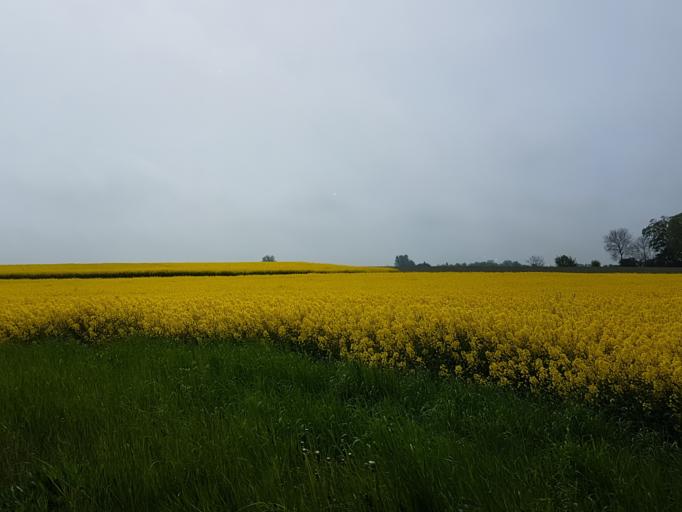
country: SE
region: Skane
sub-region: Tomelilla Kommun
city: Tomelilla
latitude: 55.4606
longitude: 14.1048
